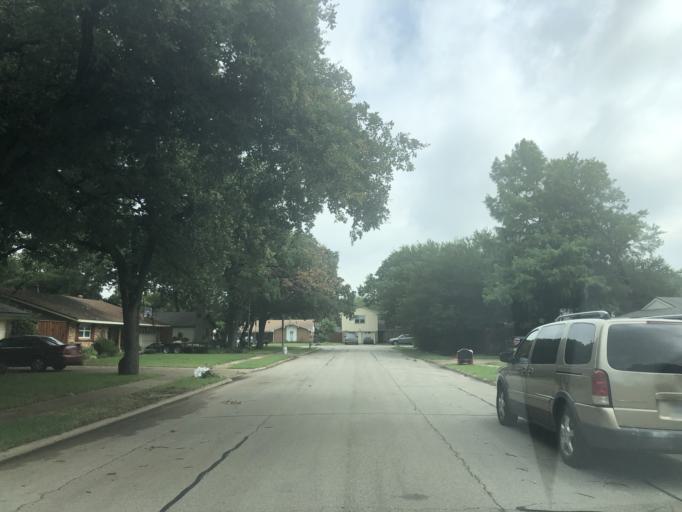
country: US
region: Texas
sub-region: Dallas County
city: Irving
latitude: 32.8056
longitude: -96.9883
